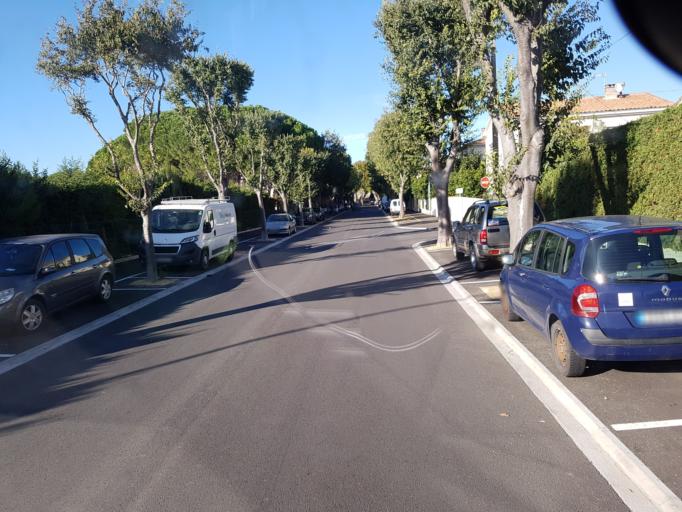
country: FR
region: Languedoc-Roussillon
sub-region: Departement de l'Aude
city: Narbonne
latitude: 43.1760
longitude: 3.0036
